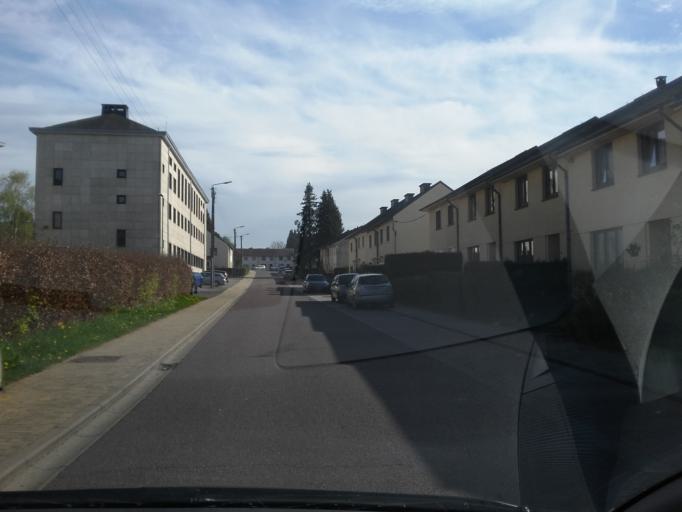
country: BE
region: Wallonia
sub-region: Province du Luxembourg
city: Arlon
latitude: 49.6845
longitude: 5.8003
